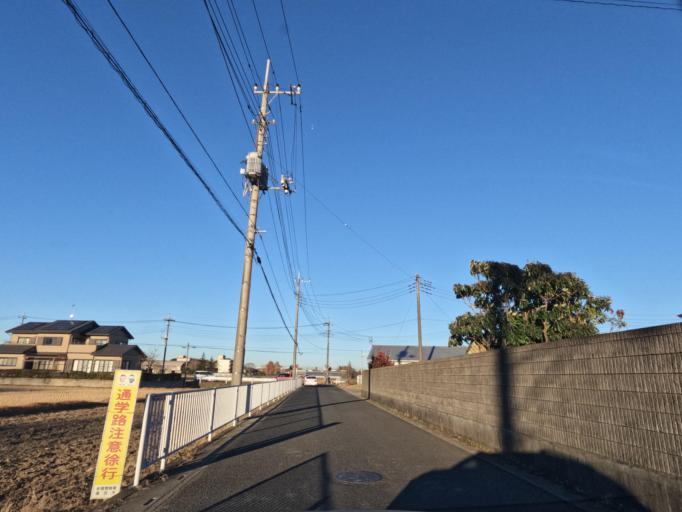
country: JP
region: Saitama
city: Hasuda
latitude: 35.9651
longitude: 139.6477
